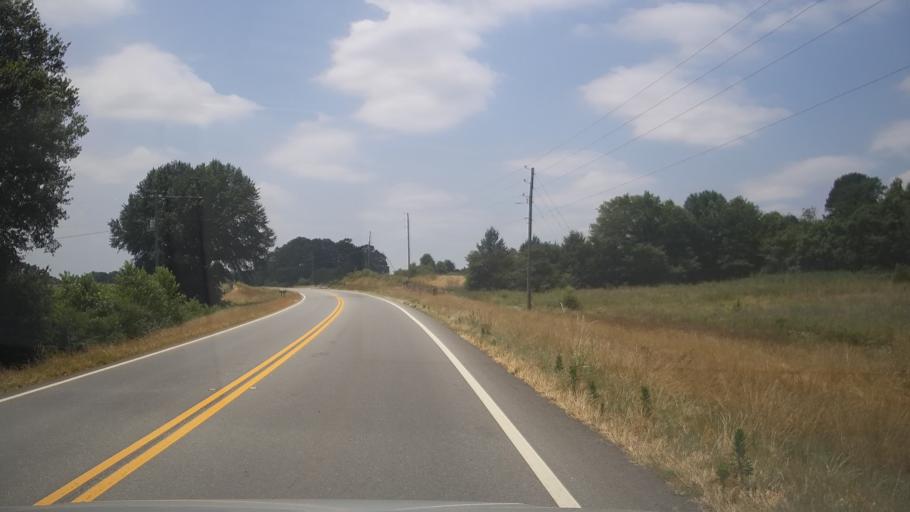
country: US
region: Georgia
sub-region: Jackson County
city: Nicholson
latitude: 34.1829
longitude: -83.3439
